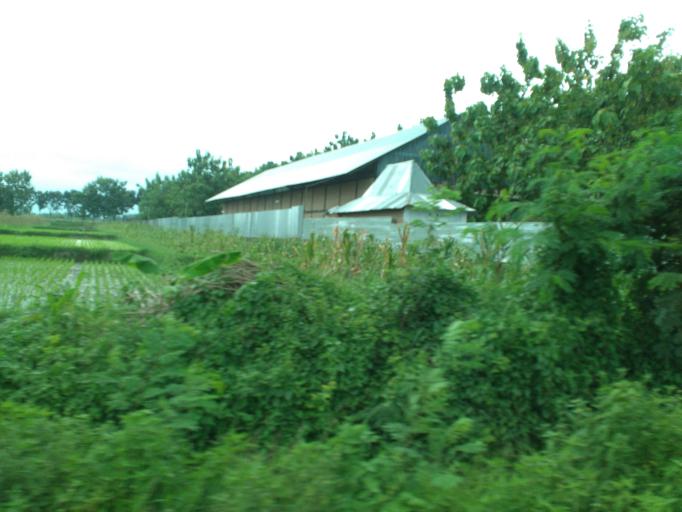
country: ID
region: Central Java
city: Ceper
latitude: -7.6844
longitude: 110.6459
